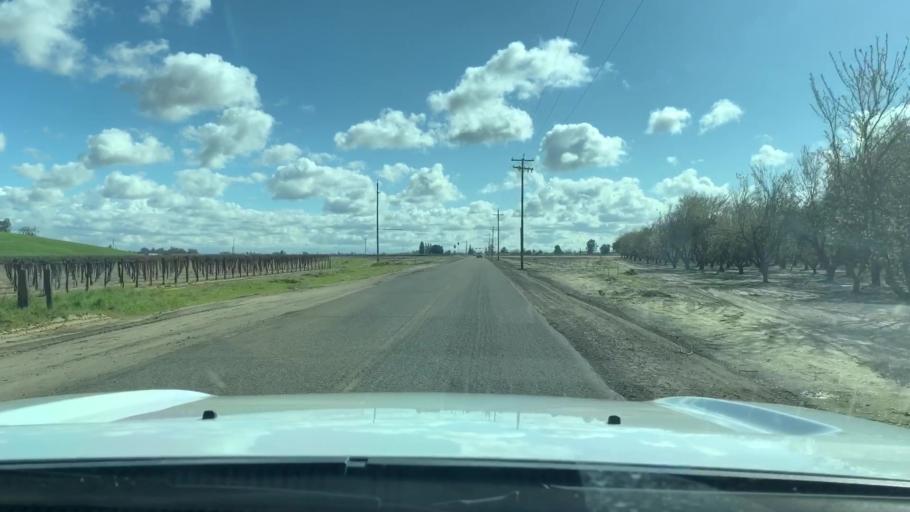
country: US
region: California
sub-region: Fresno County
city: Caruthers
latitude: 36.5472
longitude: -119.7425
